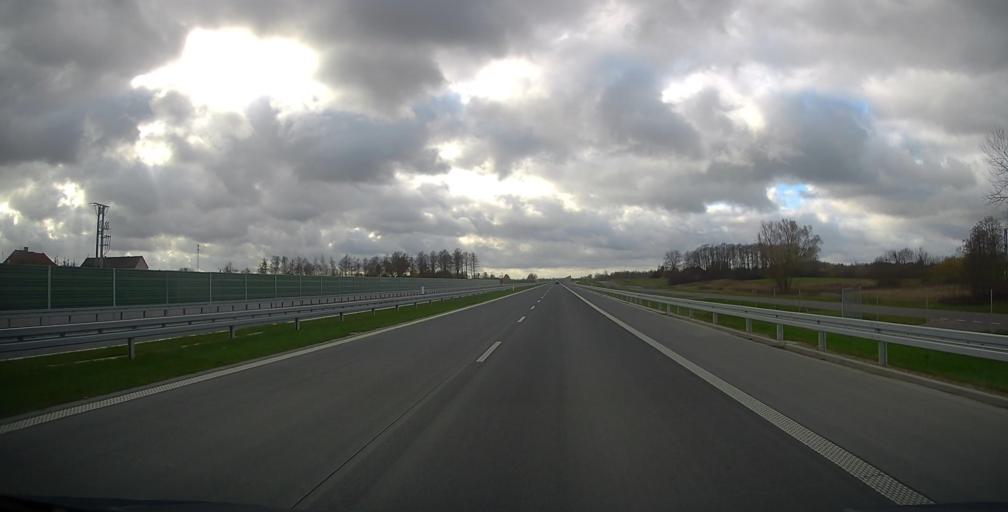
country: PL
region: Podlasie
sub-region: Powiat suwalski
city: Raczki
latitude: 53.9156
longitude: 22.7316
